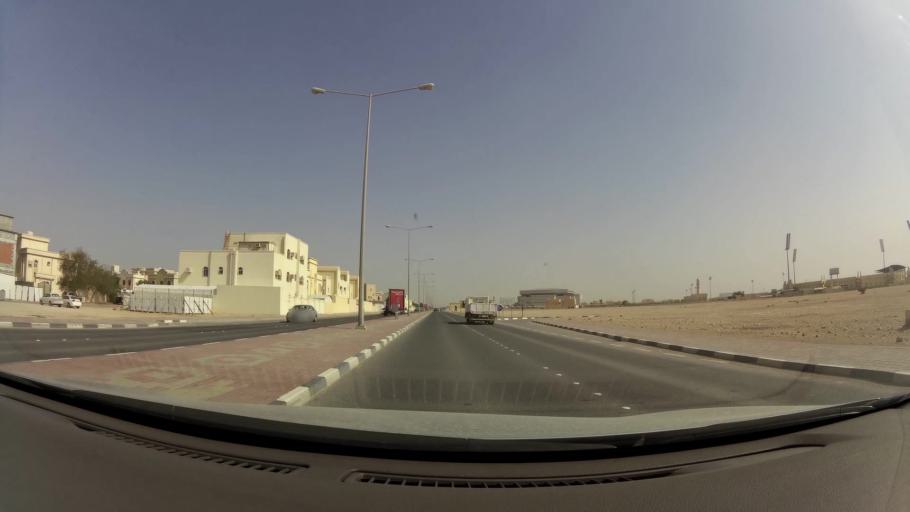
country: QA
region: Baladiyat ar Rayyan
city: Ar Rayyan
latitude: 25.3499
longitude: 51.4416
